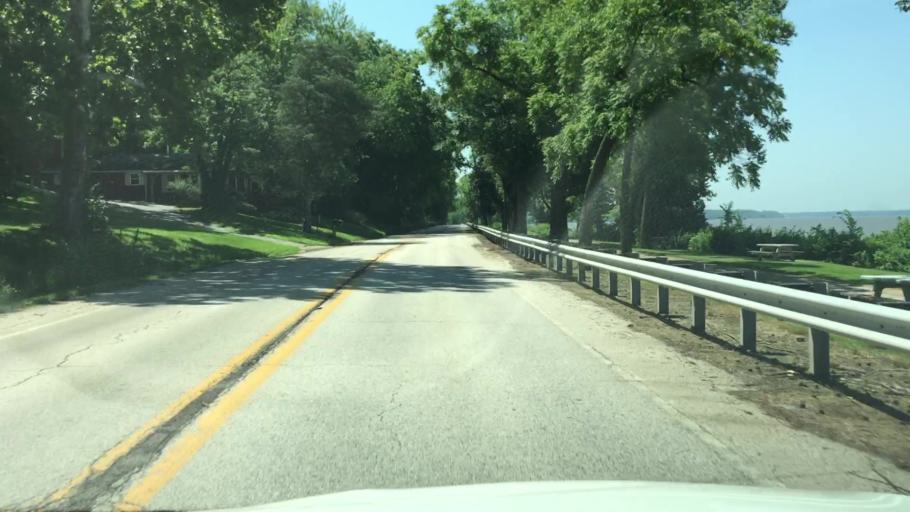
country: US
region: Illinois
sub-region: Hancock County
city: Nauvoo
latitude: 40.5082
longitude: -91.3573
